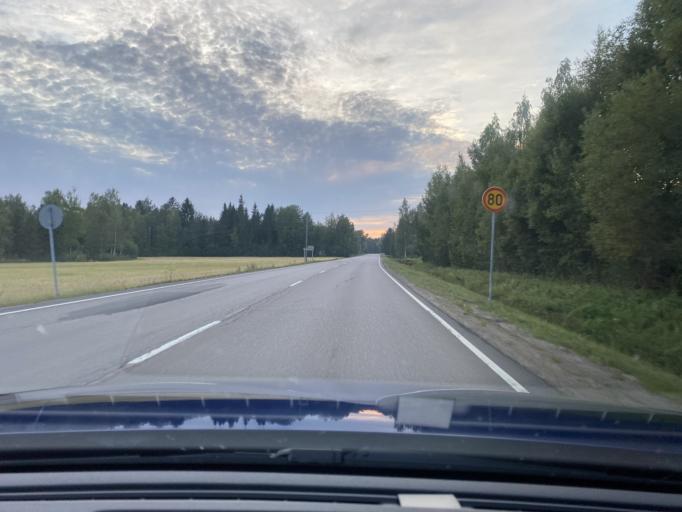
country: FI
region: Satakunta
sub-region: Pohjois-Satakunta
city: Honkajoki
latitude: 61.9213
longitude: 22.2534
